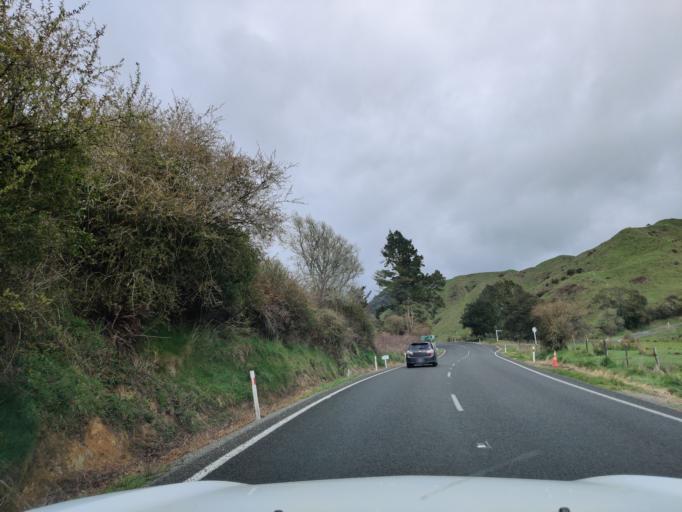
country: NZ
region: Waikato
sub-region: Otorohanga District
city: Otorohanga
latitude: -38.6176
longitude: 175.2180
